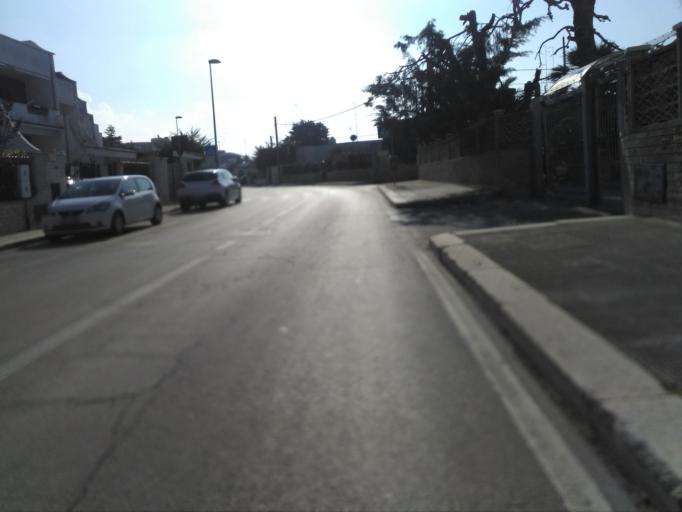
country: IT
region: Apulia
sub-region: Provincia di Bari
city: San Paolo
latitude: 41.1577
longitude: 16.7620
